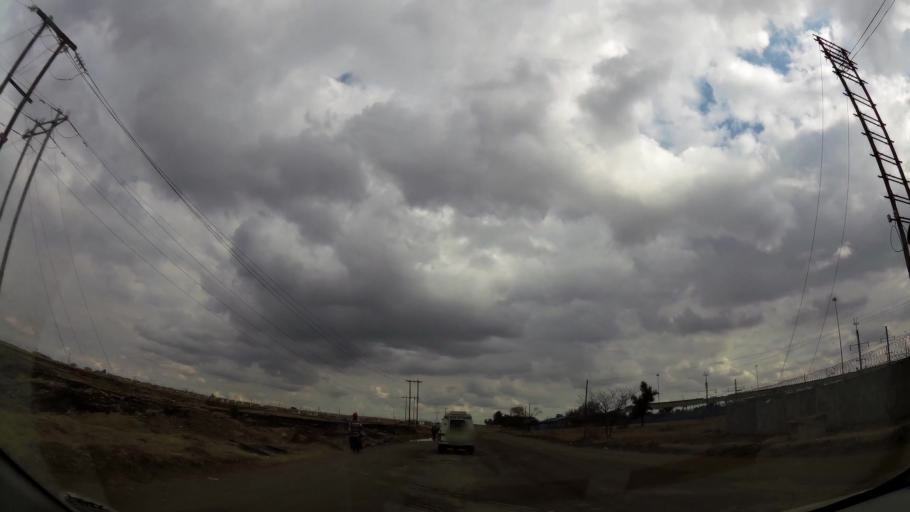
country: ZA
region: Orange Free State
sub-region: Fezile Dabi District Municipality
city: Sasolburg
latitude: -26.8537
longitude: 27.8679
